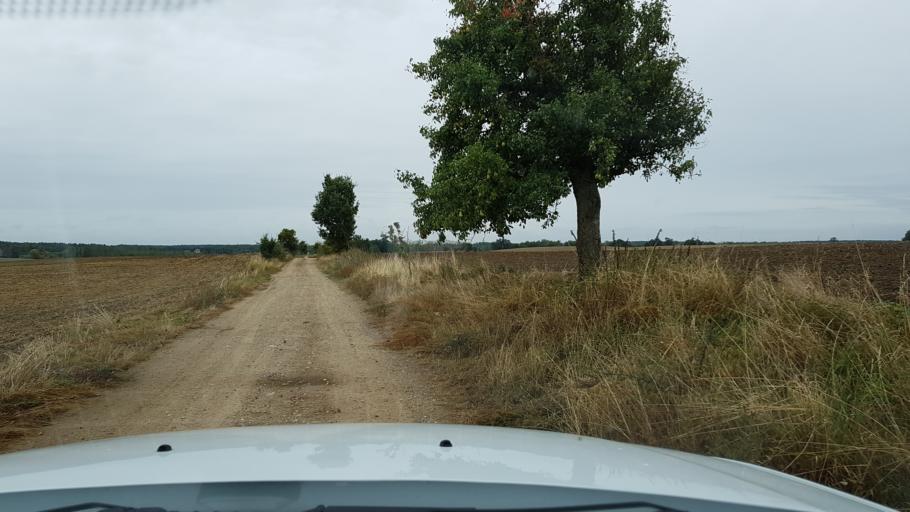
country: PL
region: West Pomeranian Voivodeship
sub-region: Powiat gryfinski
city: Chojna
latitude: 52.9047
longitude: 14.4421
